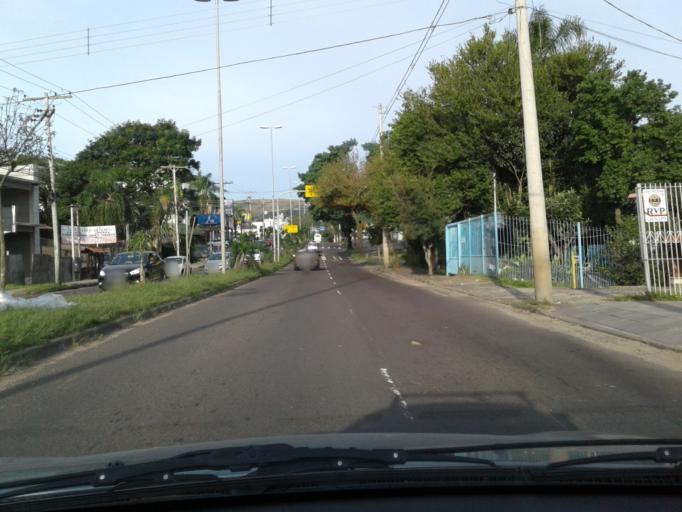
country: BR
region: Rio Grande do Sul
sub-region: Porto Alegre
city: Porto Alegre
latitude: -30.0923
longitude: -51.2348
